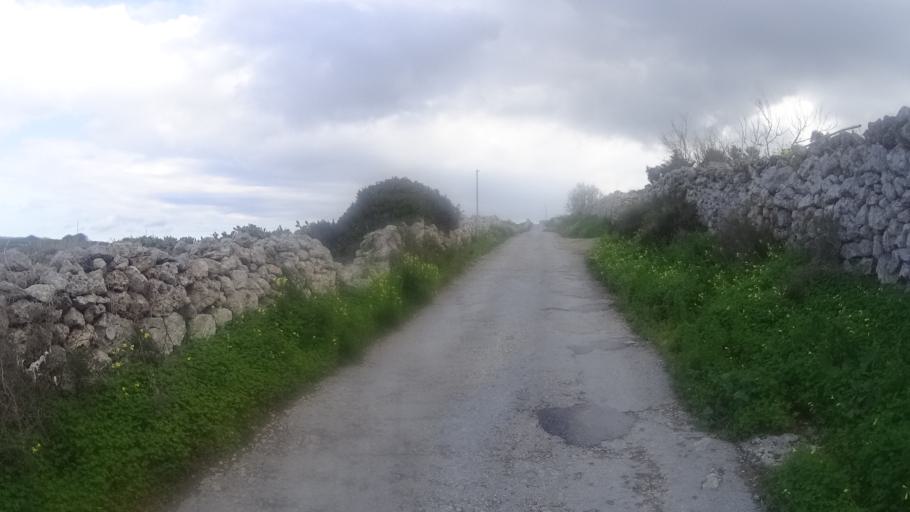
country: MT
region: L-Imgarr
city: Imgarr
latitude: 35.9019
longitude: 14.3696
